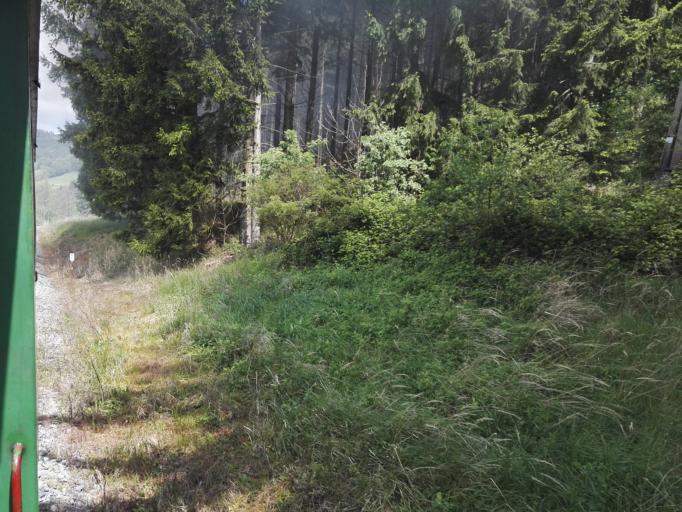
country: AT
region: Styria
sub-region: Politischer Bezirk Weiz
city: Anger
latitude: 47.2529
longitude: 15.7155
